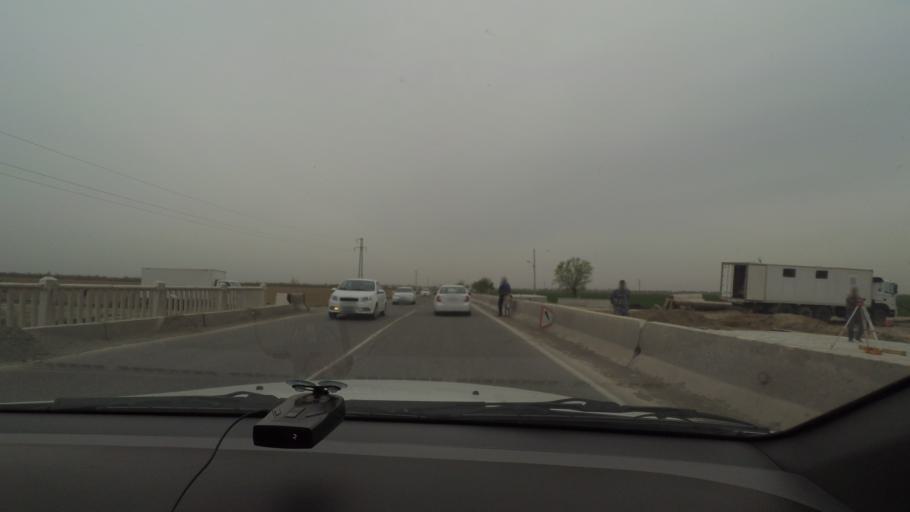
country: KZ
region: Ongtustik Qazaqstan
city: Myrzakent
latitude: 40.5601
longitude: 68.3843
